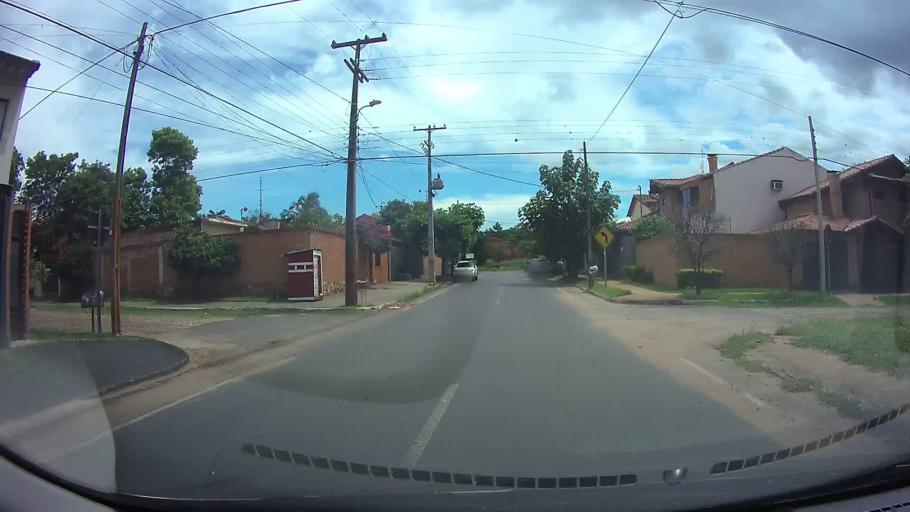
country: PY
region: Central
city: Fernando de la Mora
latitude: -25.3223
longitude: -57.5311
